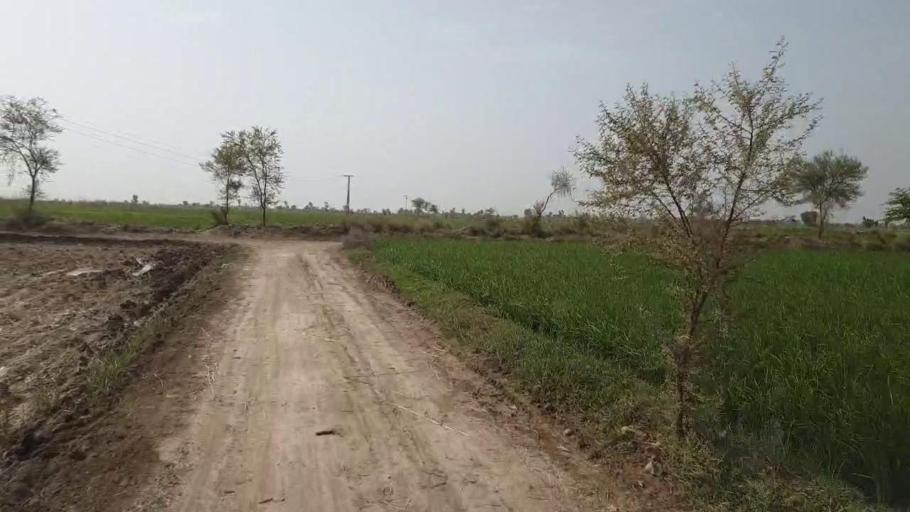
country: PK
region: Sindh
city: Daur
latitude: 26.4329
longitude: 68.1560
